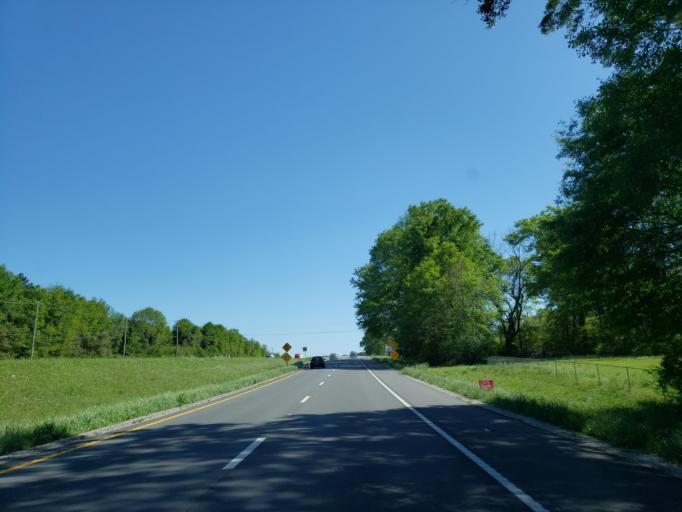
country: US
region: Mississippi
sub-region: Stone County
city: Wiggins
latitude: 30.8923
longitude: -89.1662
